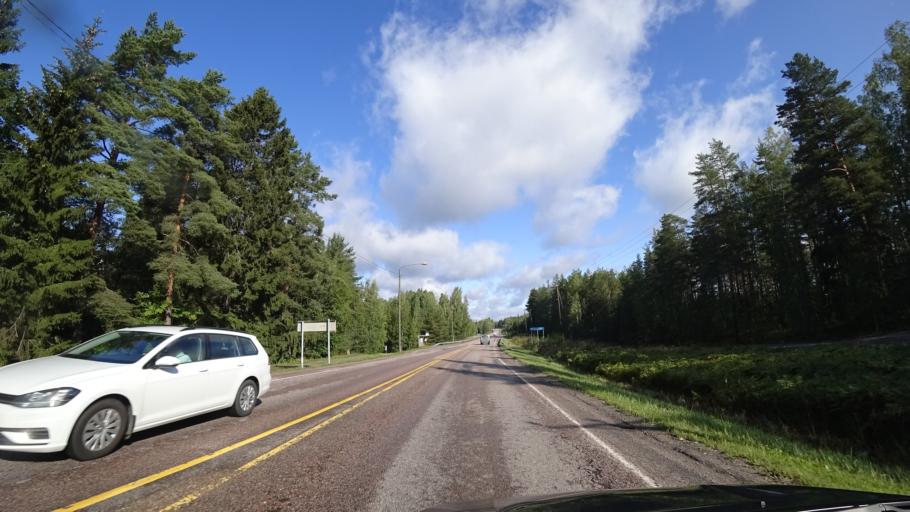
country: FI
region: Uusimaa
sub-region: Helsinki
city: Tuusula
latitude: 60.4162
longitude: 25.0010
